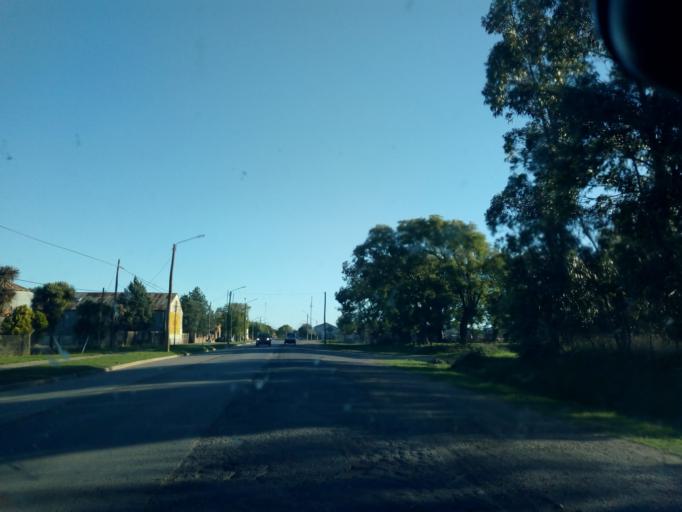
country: AR
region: Buenos Aires
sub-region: Partido de Loberia
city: Loberia
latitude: -38.1553
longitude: -58.7728
